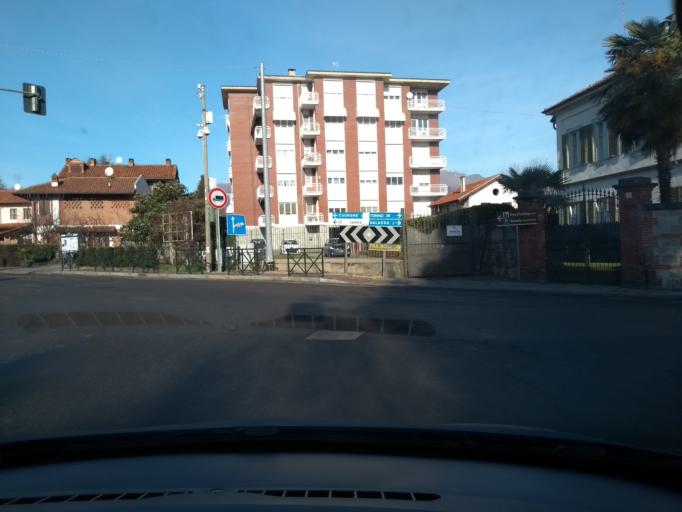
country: IT
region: Piedmont
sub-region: Provincia di Torino
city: Valperga
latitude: 45.3693
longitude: 7.6602
